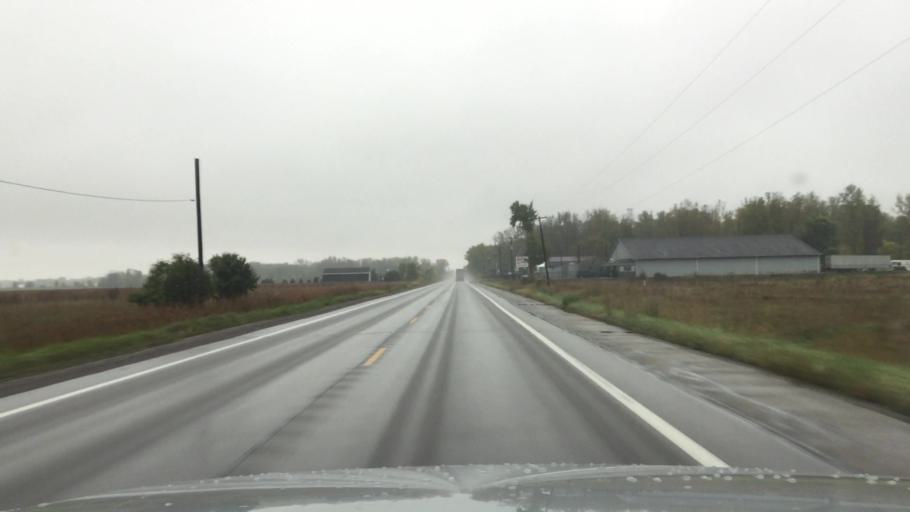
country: US
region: Michigan
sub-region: Saginaw County
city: Saginaw
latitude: 43.3776
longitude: -83.9552
